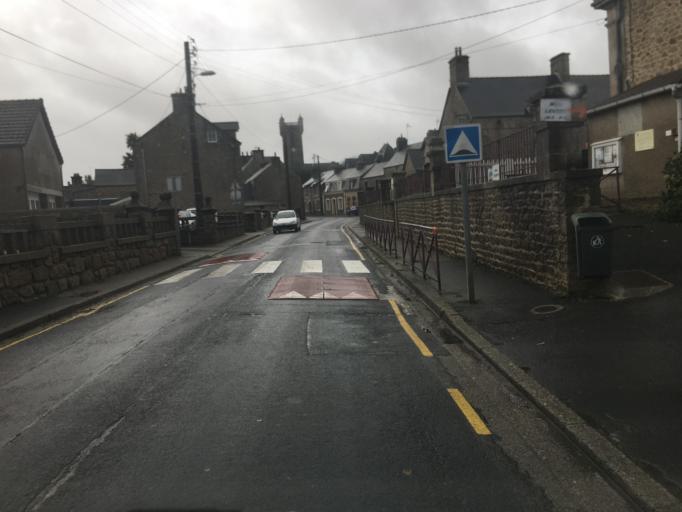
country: FR
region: Lower Normandy
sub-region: Departement de la Manche
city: Saint-Pierre-Eglise
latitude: 49.6708
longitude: -1.4048
